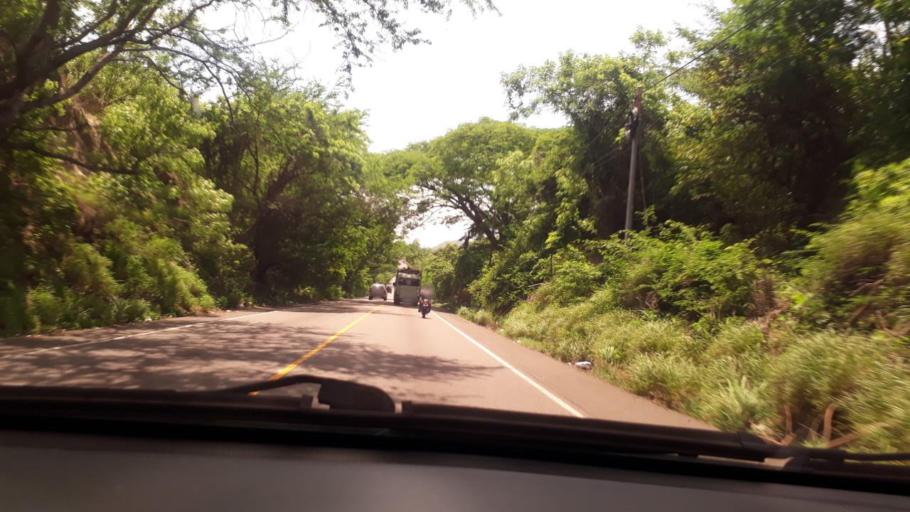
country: GT
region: Zacapa
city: Rio Hondo
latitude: 15.0547
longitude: -89.5567
